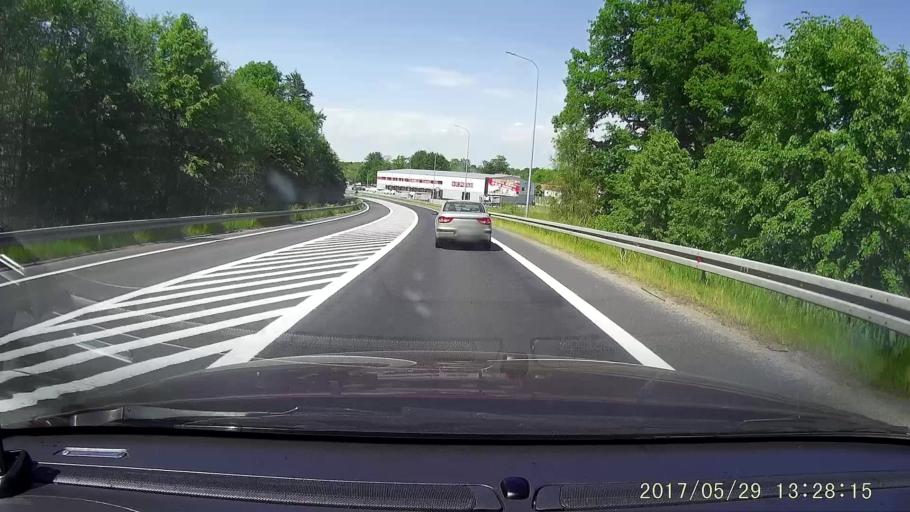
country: PL
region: Lower Silesian Voivodeship
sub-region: Powiat lubanski
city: Olszyna
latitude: 51.0627
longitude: 15.3735
